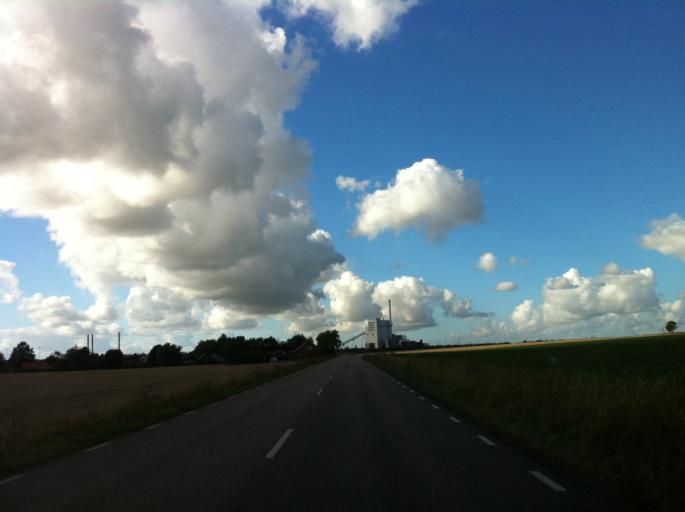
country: SE
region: Skane
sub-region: Eslovs Kommun
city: Eslov
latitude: 55.7809
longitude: 13.2832
